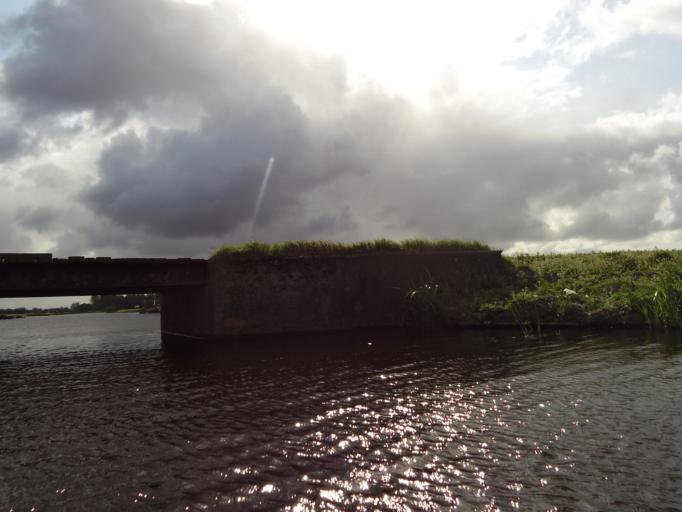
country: NL
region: South Holland
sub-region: Gemeente Wassenaar
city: Wassenaar
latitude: 52.1152
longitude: 4.3965
